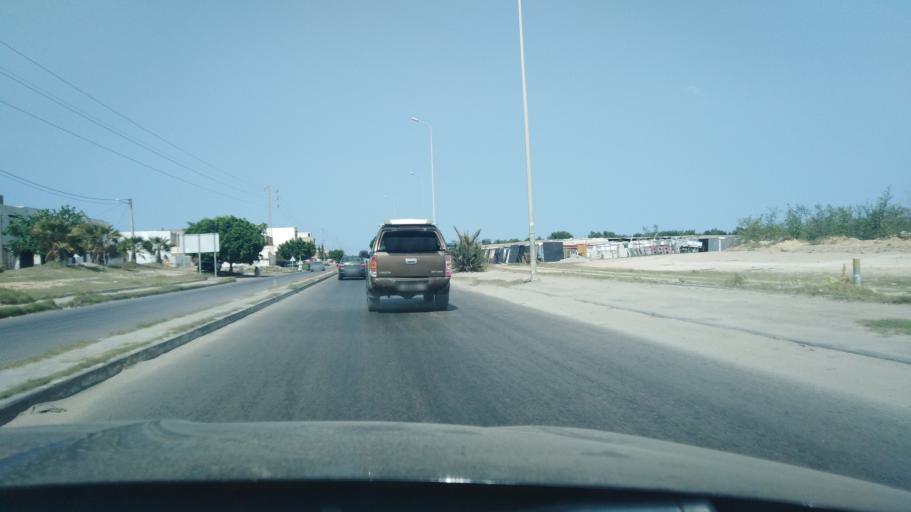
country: TN
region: Susah
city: Sousse
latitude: 35.7948
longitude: 10.5994
